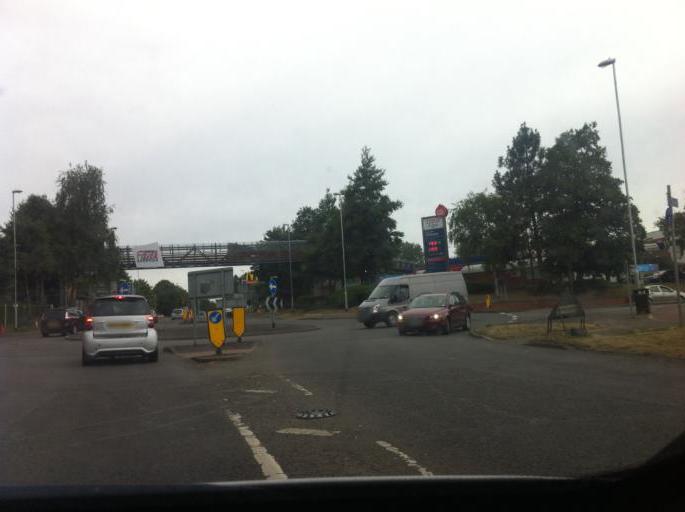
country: GB
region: England
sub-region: Northamptonshire
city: Northampton
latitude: 52.2556
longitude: -0.8325
